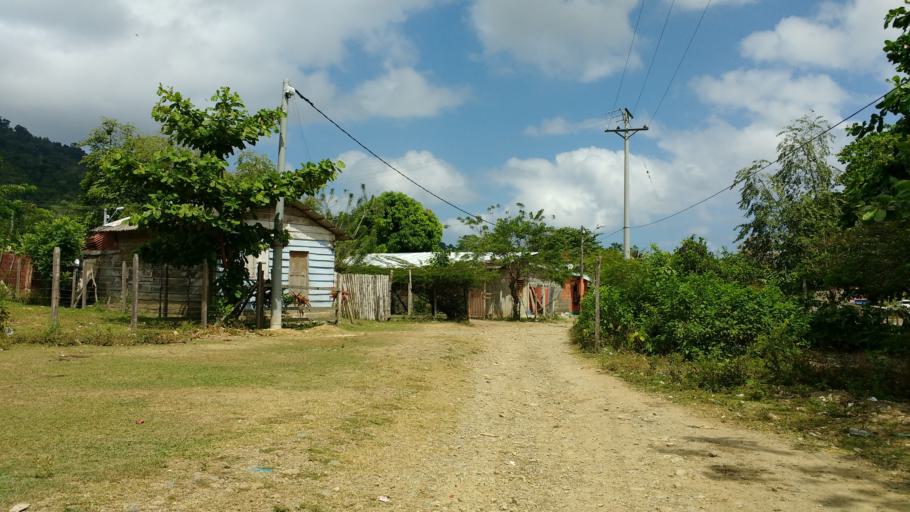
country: PA
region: Guna Yala
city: Puerto Obaldia
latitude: 8.6337
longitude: -77.3506
